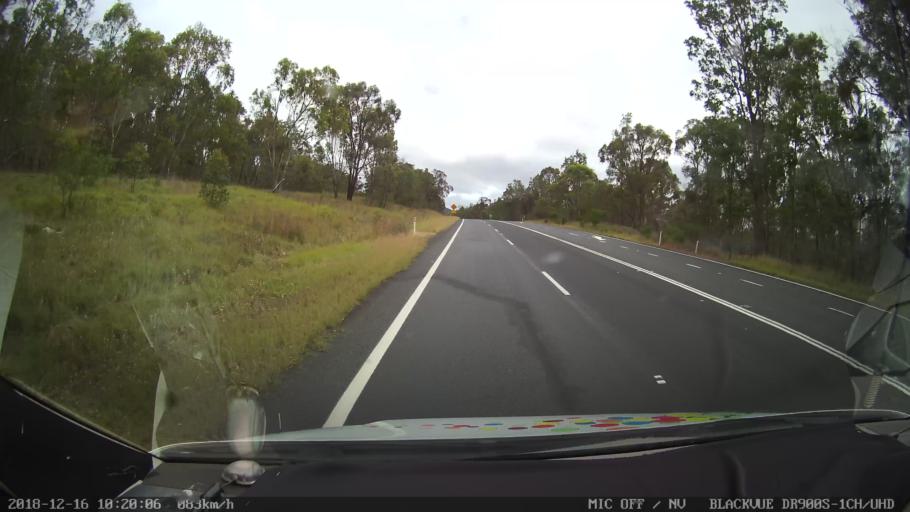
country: AU
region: New South Wales
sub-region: Tenterfield Municipality
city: Carrolls Creek
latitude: -29.2245
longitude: 152.0094
